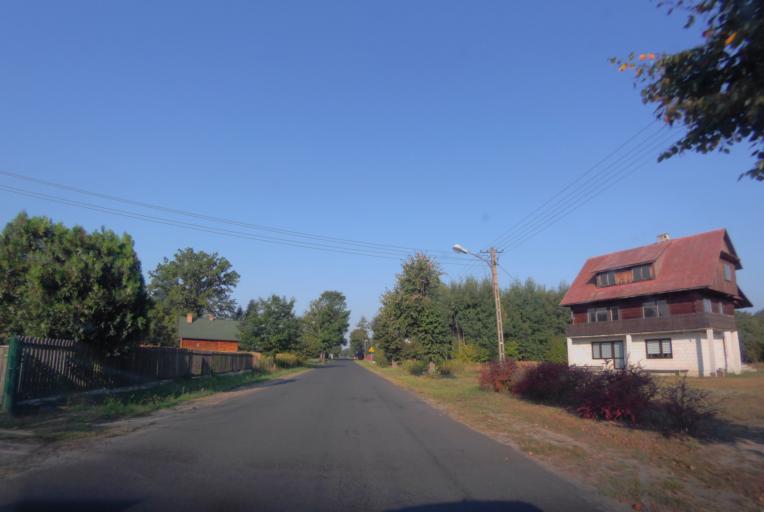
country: PL
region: Subcarpathian Voivodeship
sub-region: Powiat nizanski
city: Harasiuki
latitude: 50.5436
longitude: 22.5423
